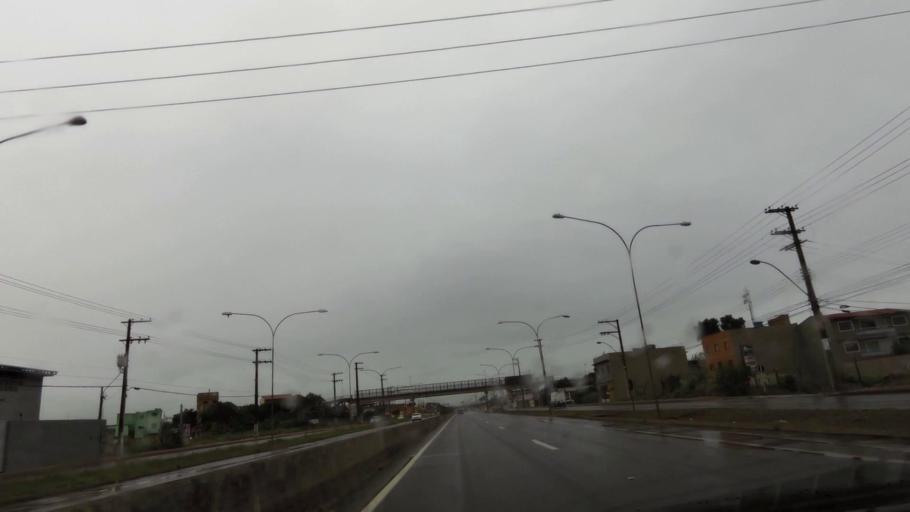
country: BR
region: Espirito Santo
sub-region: Vila Velha
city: Vila Velha
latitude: -20.4336
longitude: -40.3314
